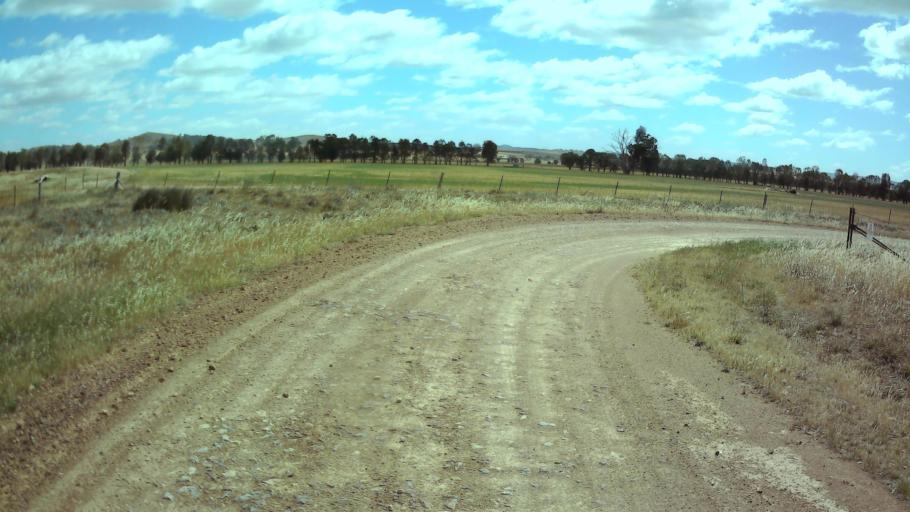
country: AU
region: New South Wales
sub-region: Weddin
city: Grenfell
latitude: -33.9964
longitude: 148.2893
